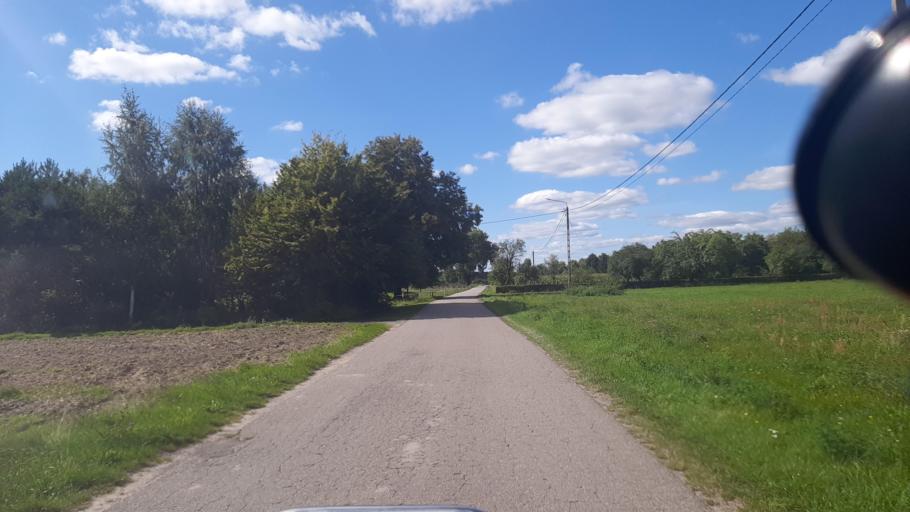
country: PL
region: Lublin Voivodeship
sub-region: Powiat lubelski
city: Garbow
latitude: 51.4065
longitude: 22.4011
